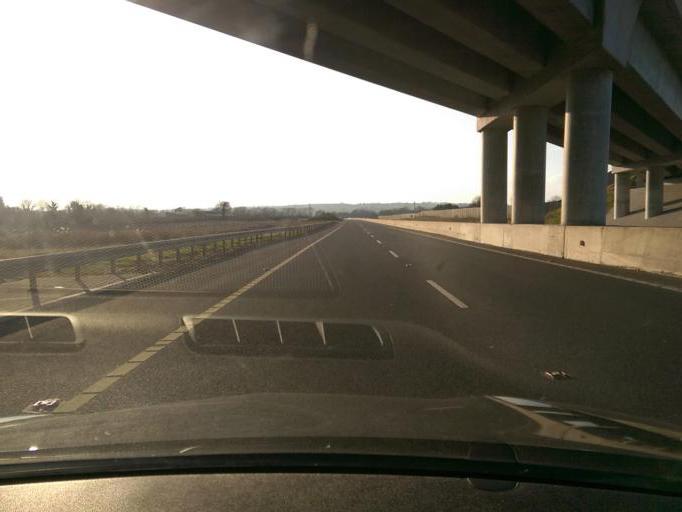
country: IE
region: Munster
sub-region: North Tipperary
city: Roscrea
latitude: 52.9256
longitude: -7.7500
